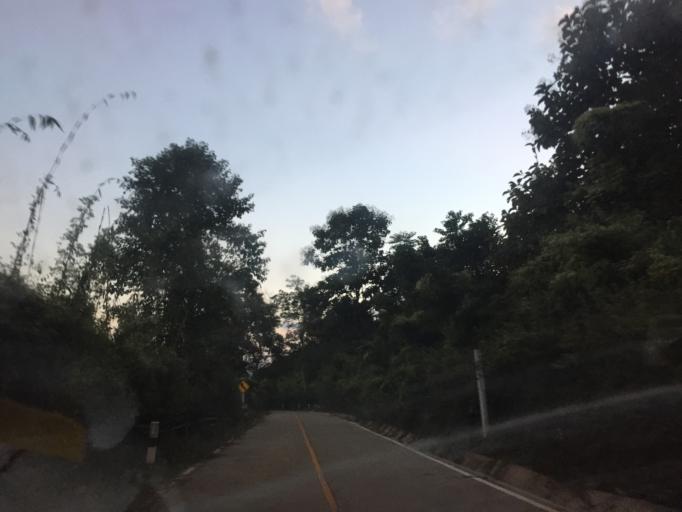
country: TH
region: Chiang Mai
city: Samoeng
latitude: 18.9936
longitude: 98.7182
